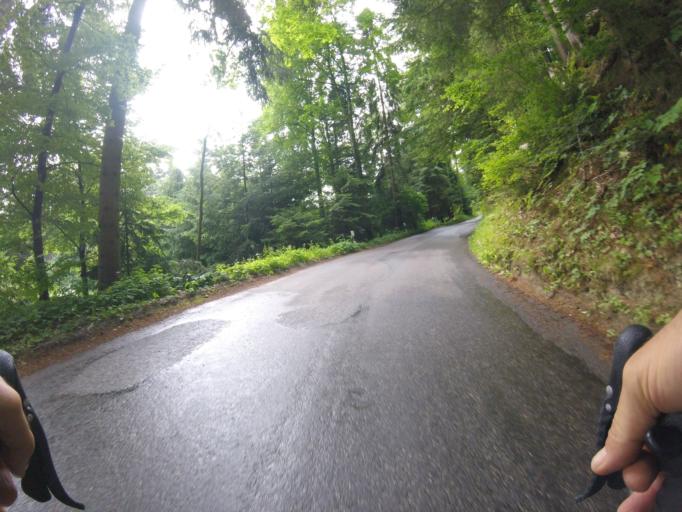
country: CH
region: Bern
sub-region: Emmental District
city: Krauchthal
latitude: 47.0094
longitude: 7.5980
